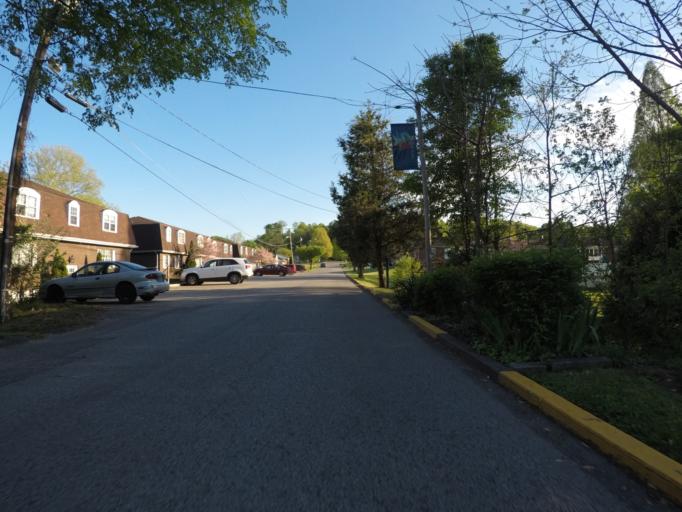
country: US
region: West Virginia
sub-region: Wayne County
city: Ceredo
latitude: 38.3943
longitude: -82.5602
